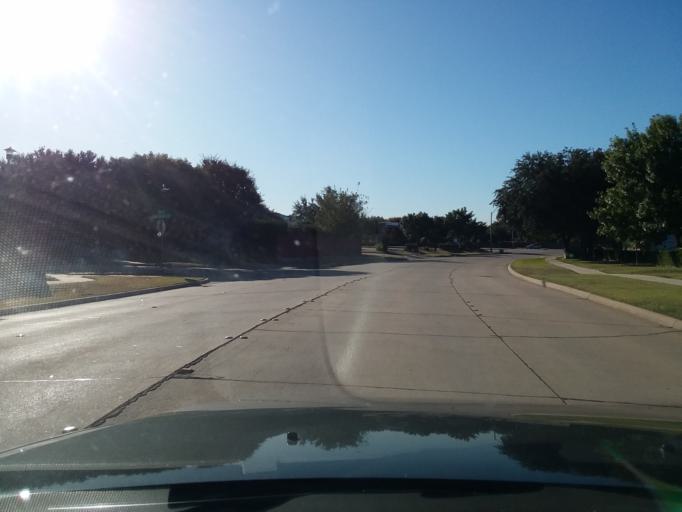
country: US
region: Texas
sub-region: Denton County
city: Lewisville
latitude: 33.0583
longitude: -97.0239
